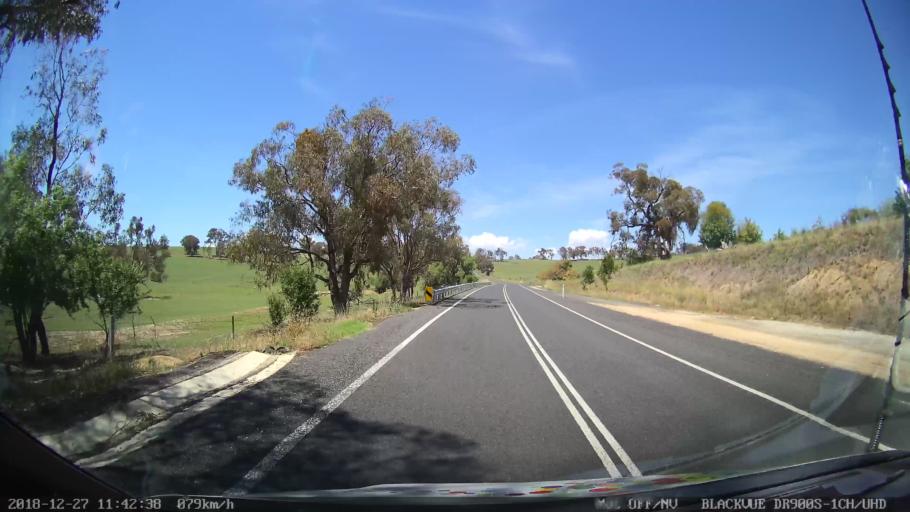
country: AU
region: New South Wales
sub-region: Bathurst Regional
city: Perthville
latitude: -33.5509
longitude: 149.4779
